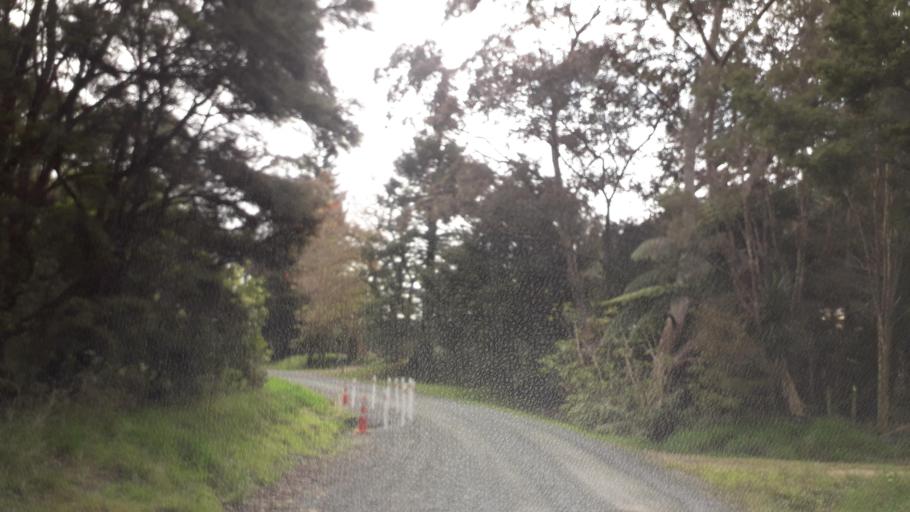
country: NZ
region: Northland
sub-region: Far North District
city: Taipa
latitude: -35.0942
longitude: 173.5312
